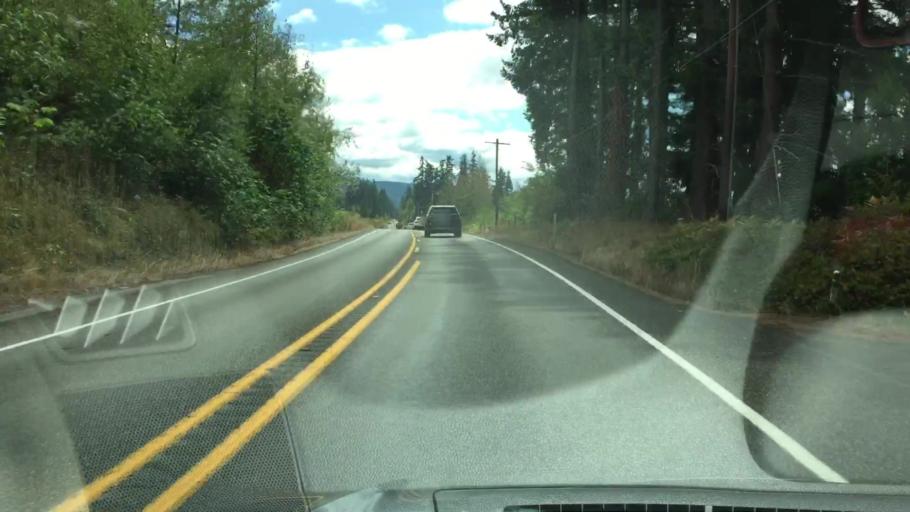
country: US
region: Washington
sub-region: Pierce County
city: Eatonville
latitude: 46.9069
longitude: -122.2979
